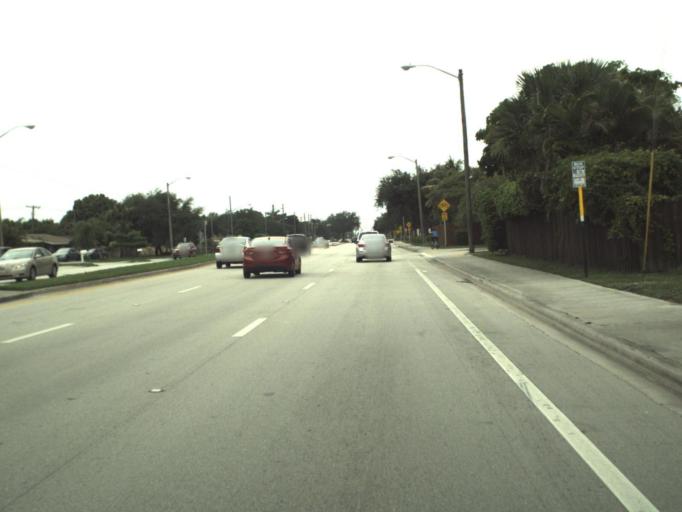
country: US
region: Florida
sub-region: Palm Beach County
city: North Palm Beach
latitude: 26.8137
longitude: -80.1063
